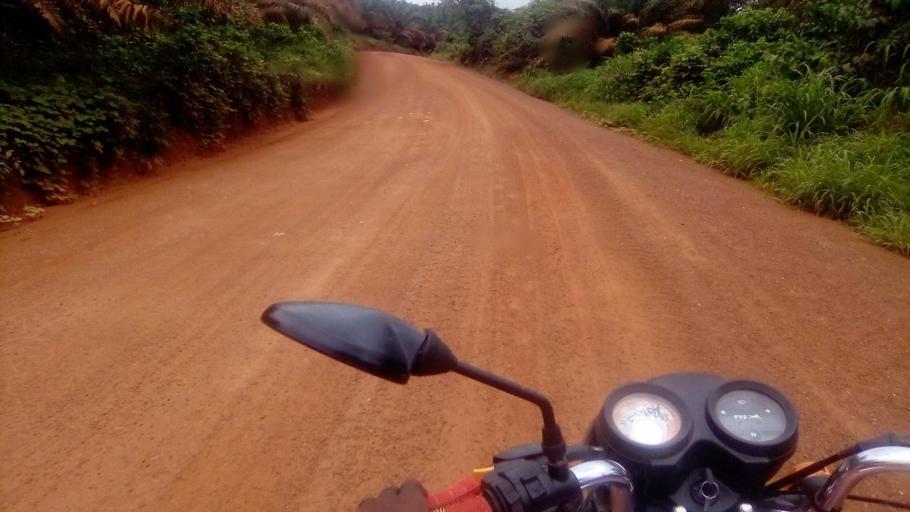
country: SL
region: Southern Province
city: Tongole
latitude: 7.4401
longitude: -11.8641
